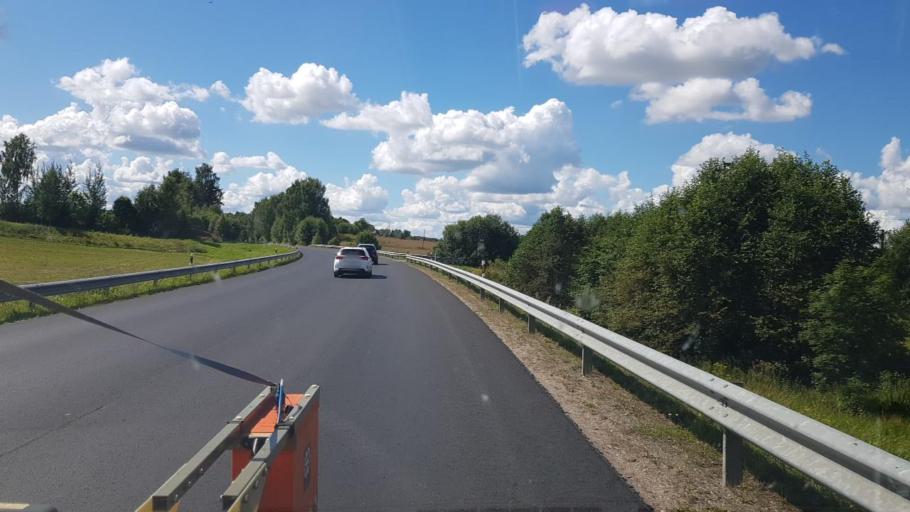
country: EE
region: Viljandimaa
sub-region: Viiratsi vald
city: Viiratsi
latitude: 58.3942
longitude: 25.6991
